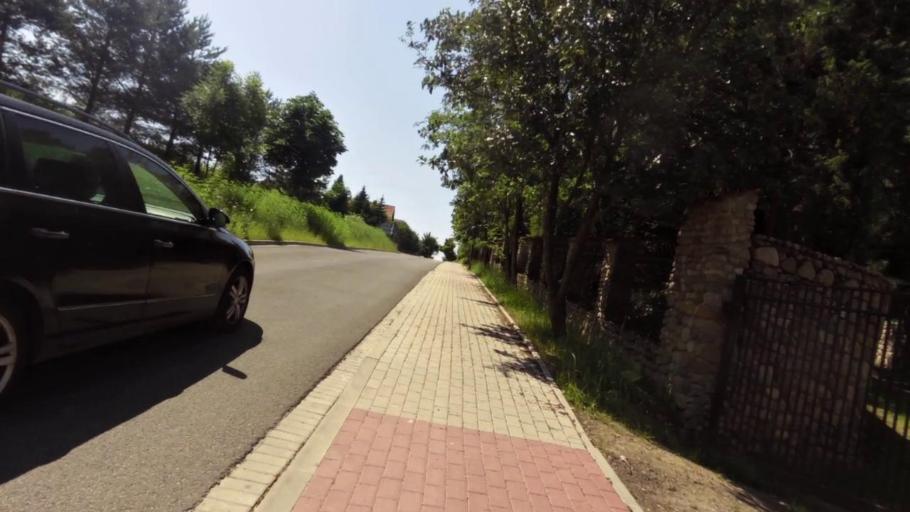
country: PL
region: West Pomeranian Voivodeship
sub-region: Powiat swidwinski
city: Polczyn-Zdroj
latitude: 53.7757
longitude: 16.1086
